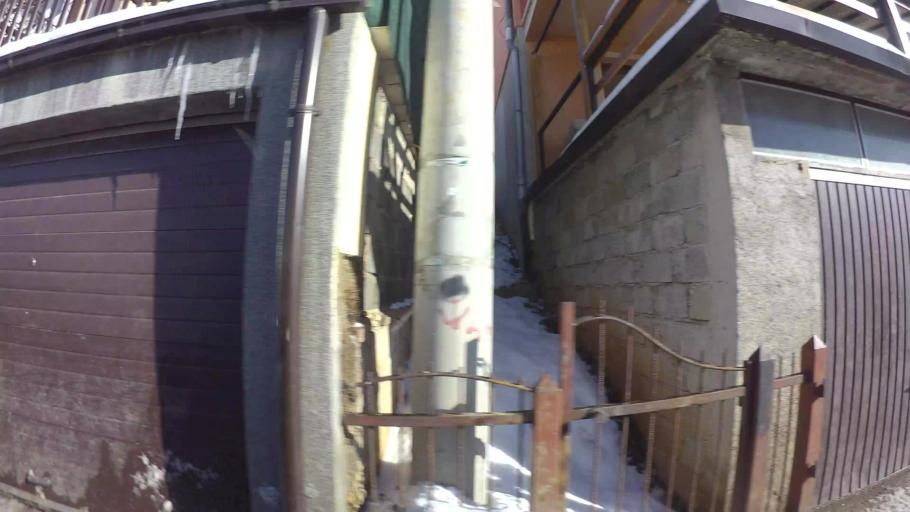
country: BA
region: Federation of Bosnia and Herzegovina
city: Kobilja Glava
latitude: 43.8743
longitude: 18.4230
